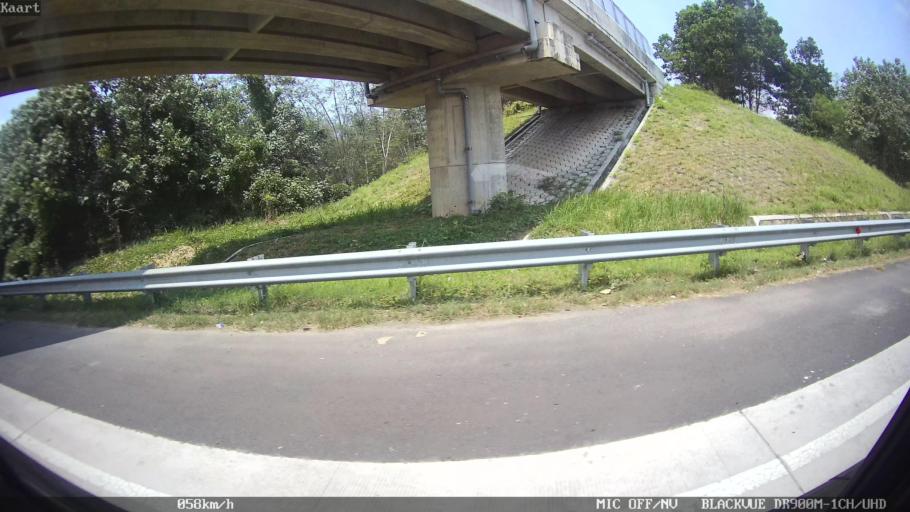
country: ID
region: Lampung
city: Kedaton
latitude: -5.3778
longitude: 105.3301
